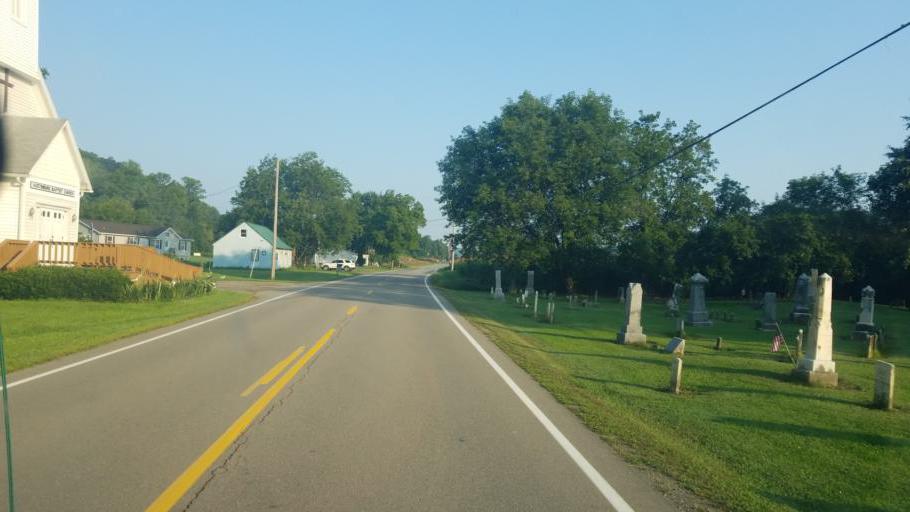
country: US
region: Pennsylvania
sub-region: Tioga County
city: Westfield
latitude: 41.9951
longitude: -77.4979
